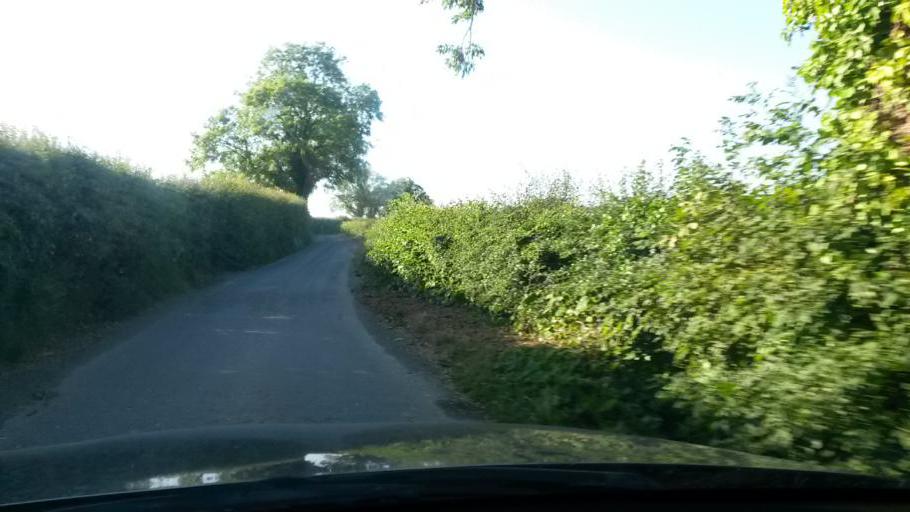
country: IE
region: Leinster
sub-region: Fingal County
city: Swords
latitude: 53.4997
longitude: -6.2910
